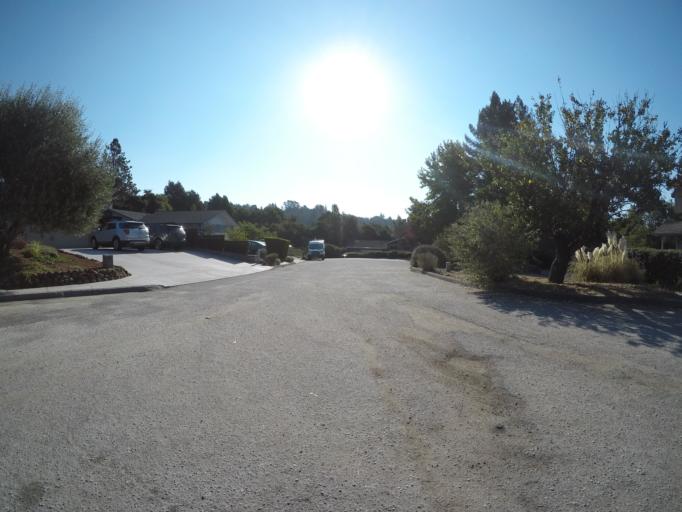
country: US
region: California
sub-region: Santa Cruz County
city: Scotts Valley
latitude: 37.0449
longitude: -122.0202
